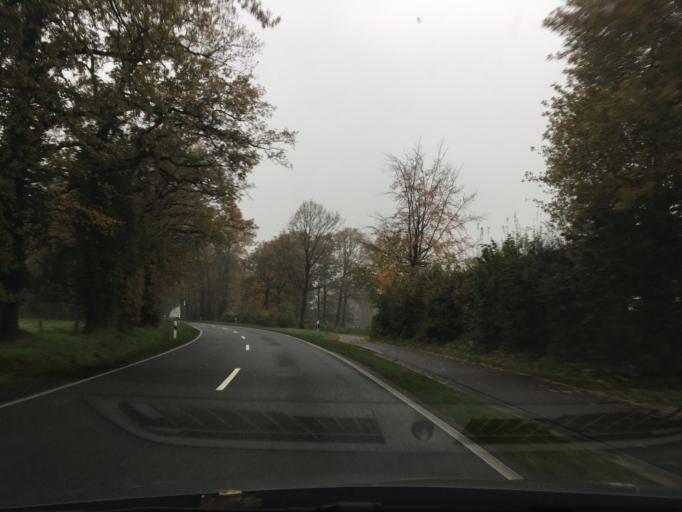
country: DE
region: North Rhine-Westphalia
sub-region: Regierungsbezirk Munster
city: Ahaus
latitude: 52.0804
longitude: 6.9380
